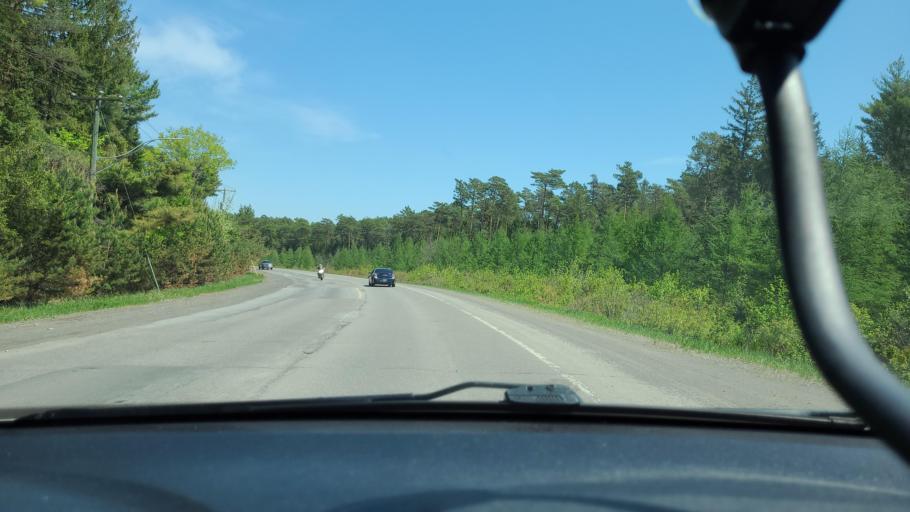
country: CA
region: Quebec
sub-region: Laurentides
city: Lachute
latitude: 45.6627
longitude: -74.2526
